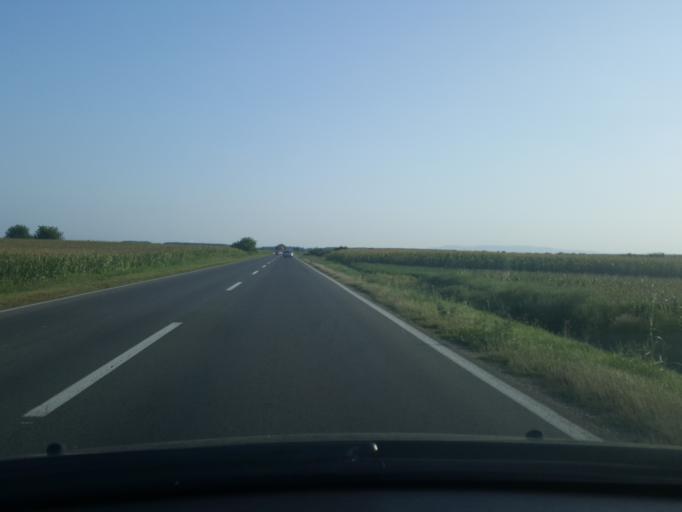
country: RS
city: Klenak
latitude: 44.7950
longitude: 19.7276
